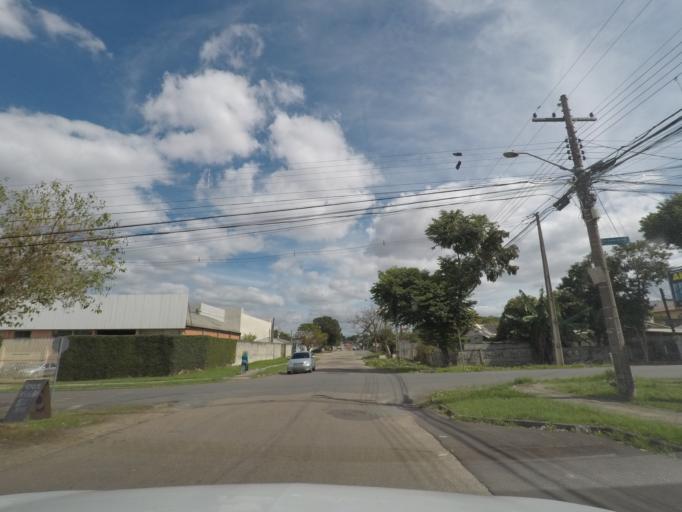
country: BR
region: Parana
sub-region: Sao Jose Dos Pinhais
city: Sao Jose dos Pinhais
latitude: -25.5145
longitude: -49.2270
